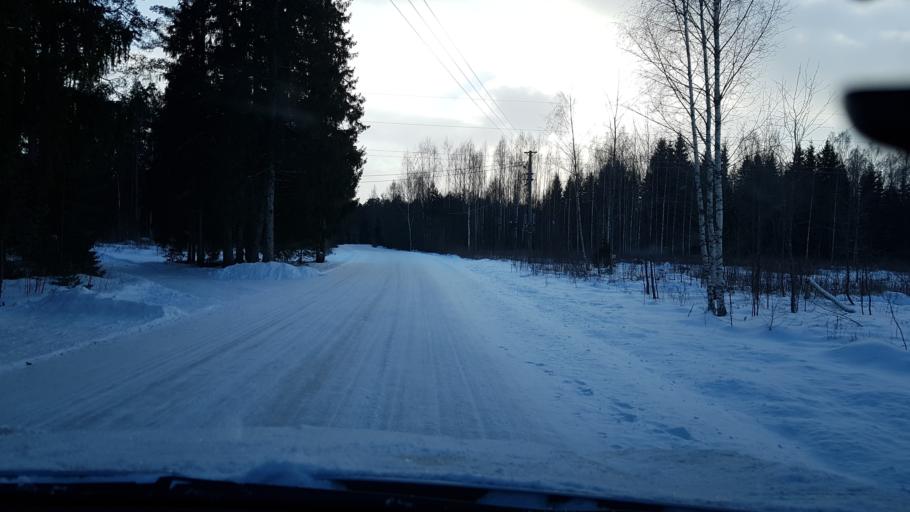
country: EE
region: Harju
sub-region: Nissi vald
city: Turba
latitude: 59.2135
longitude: 24.1412
